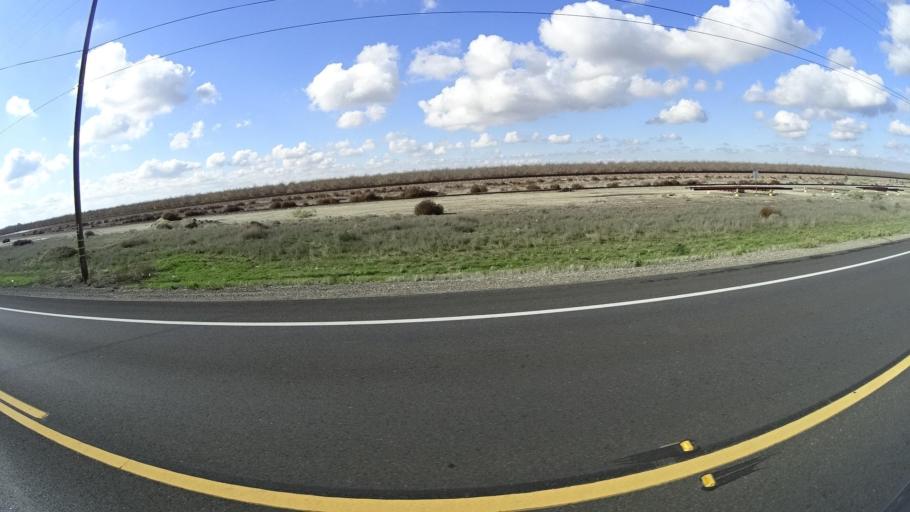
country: US
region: California
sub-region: Kern County
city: Wasco
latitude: 35.6784
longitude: -119.3300
